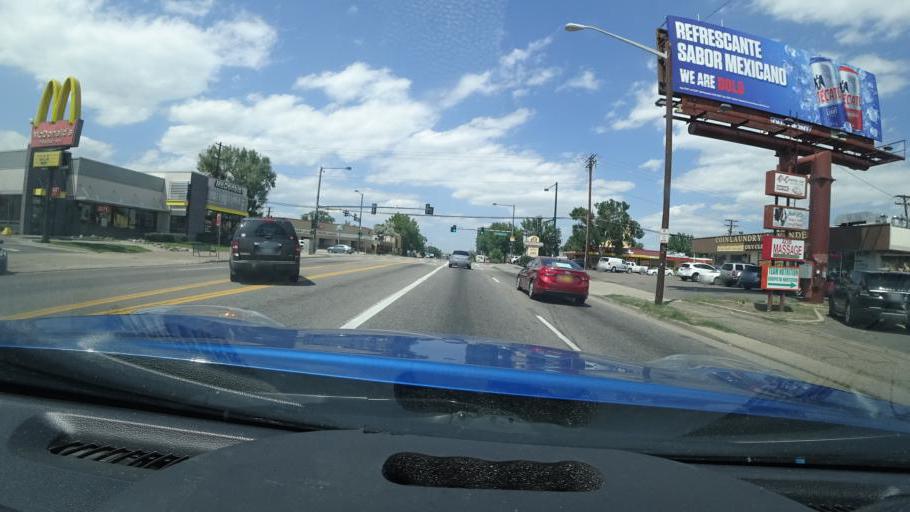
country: US
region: Colorado
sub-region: Arapahoe County
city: Sheridan
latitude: 39.6817
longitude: -105.0250
